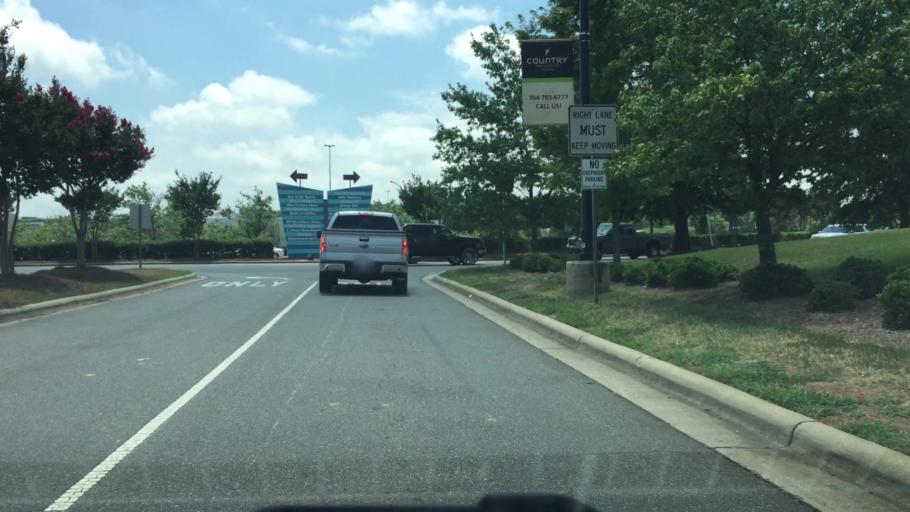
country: US
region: North Carolina
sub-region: Cabarrus County
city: Harrisburg
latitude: 35.3730
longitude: -80.7249
